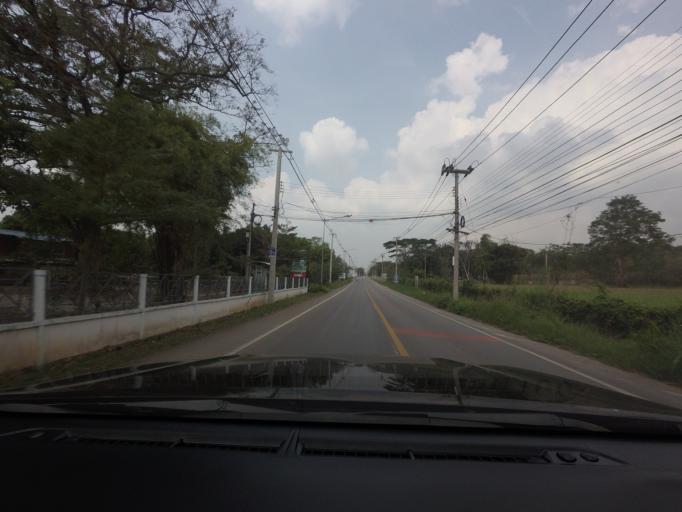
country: TH
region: Sara Buri
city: Muak Lek
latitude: 14.6035
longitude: 101.2141
